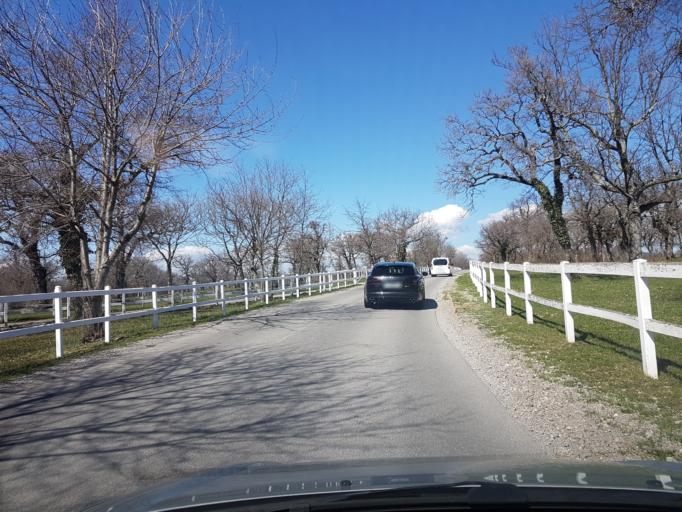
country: SI
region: Sezana
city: Sezana
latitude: 45.6667
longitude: 13.8875
